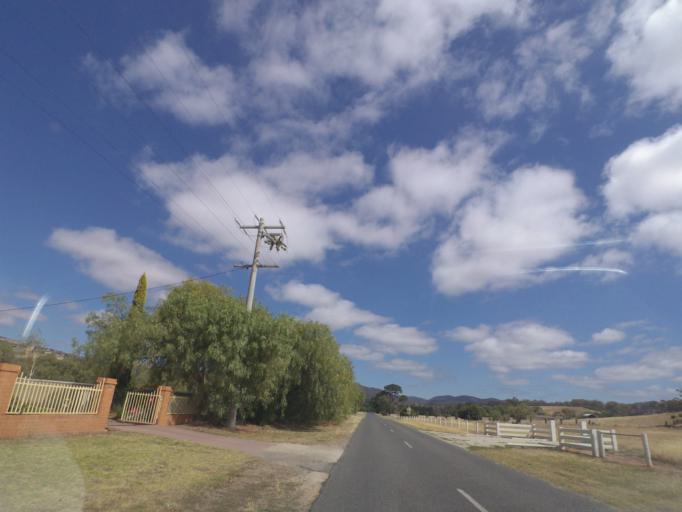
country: AU
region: Victoria
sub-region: Moorabool
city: Bacchus Marsh
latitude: -37.6430
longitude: 144.4413
